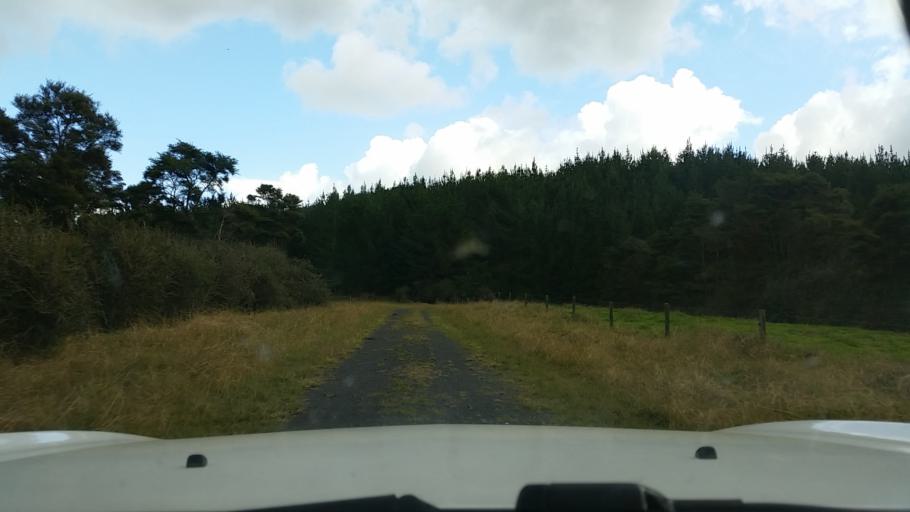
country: NZ
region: Waikato
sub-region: Hauraki District
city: Ngatea
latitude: -37.4372
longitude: 175.4713
